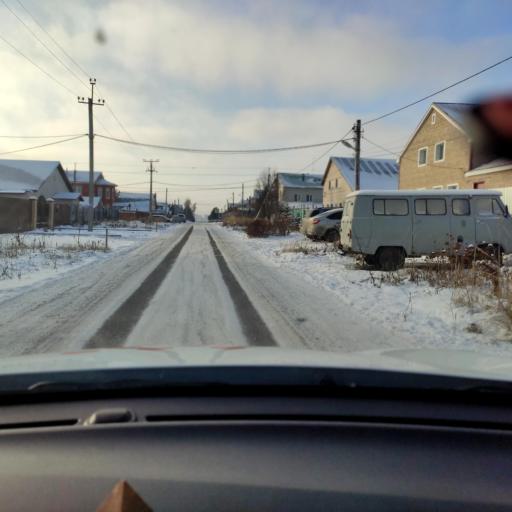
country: RU
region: Tatarstan
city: Vysokaya Gora
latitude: 55.8180
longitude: 49.2568
